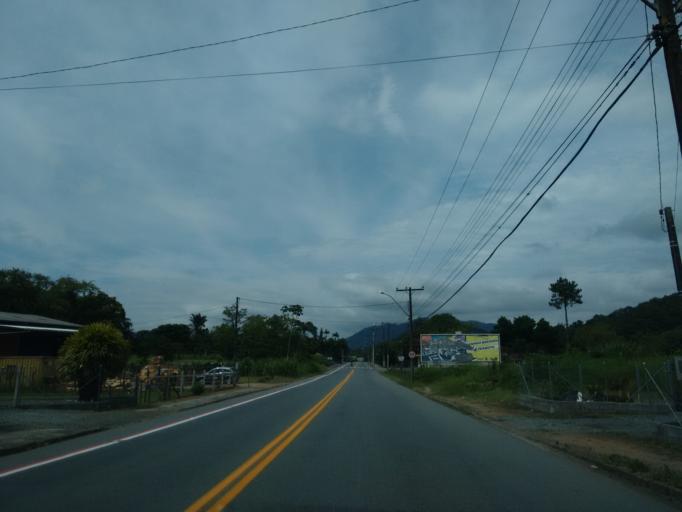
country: BR
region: Santa Catarina
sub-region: Pomerode
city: Pomerode
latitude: -26.6949
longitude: -49.1588
